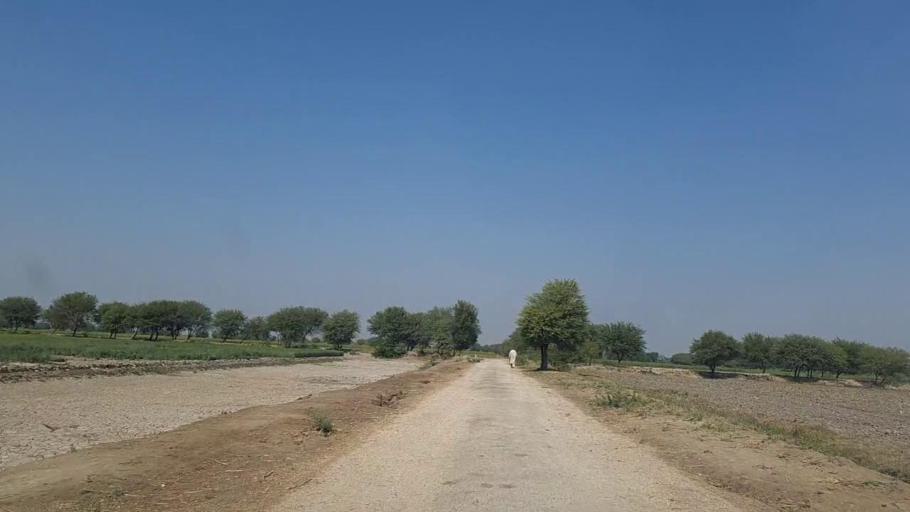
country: PK
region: Sindh
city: Naukot
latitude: 24.8782
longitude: 69.3839
